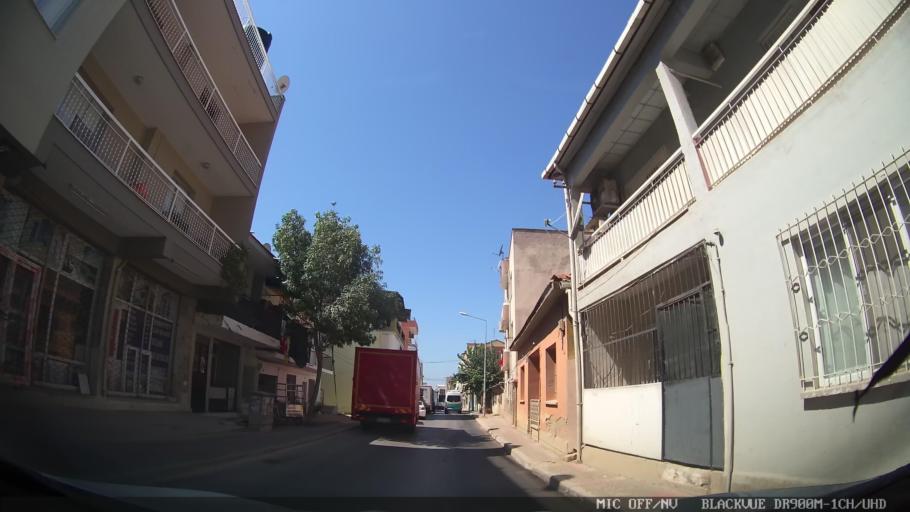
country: TR
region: Izmir
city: Karsiyaka
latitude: 38.4974
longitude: 27.0673
